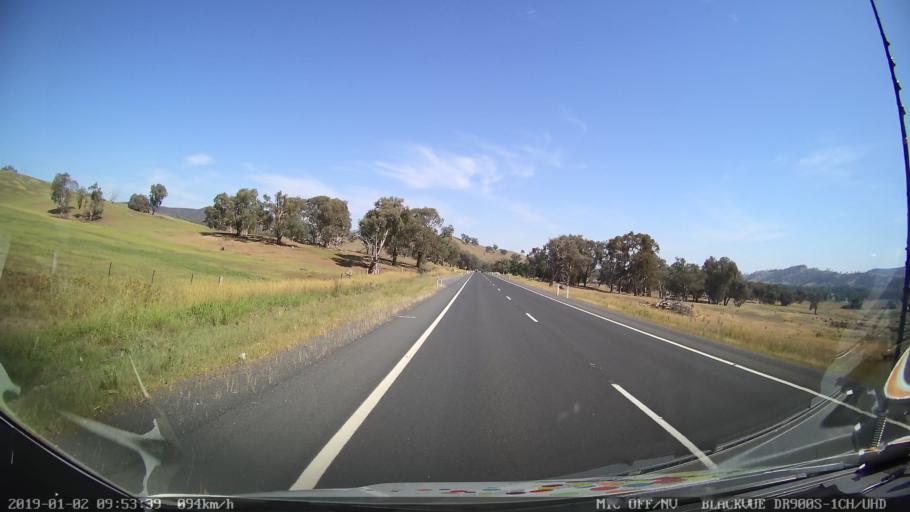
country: AU
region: New South Wales
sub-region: Tumut Shire
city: Tumut
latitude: -35.2454
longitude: 148.2012
